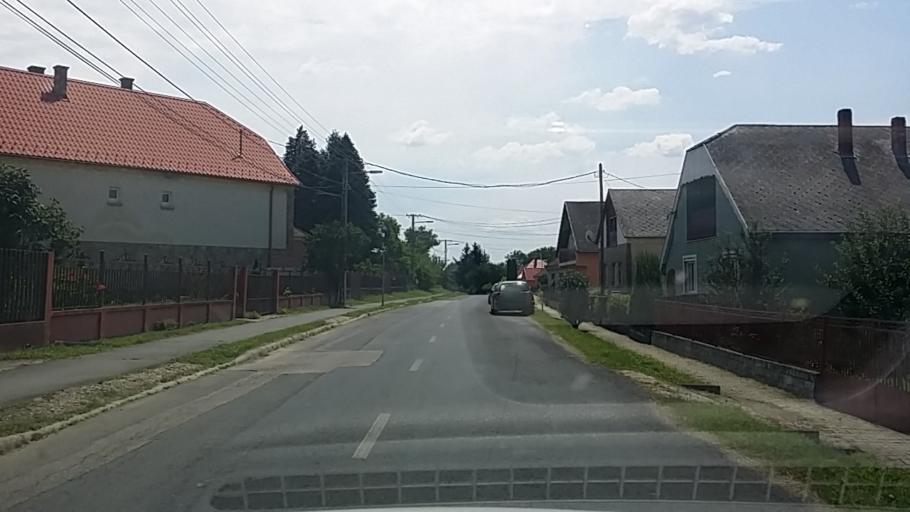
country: HR
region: Medimurska
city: Kotoriba
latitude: 46.3877
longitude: 16.8261
